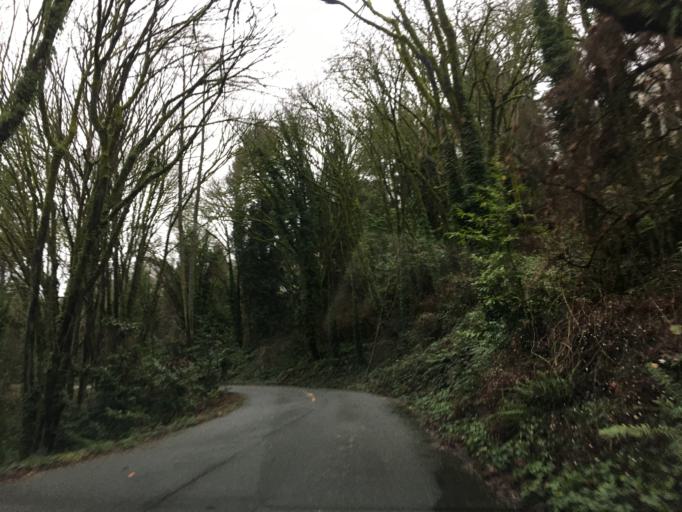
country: US
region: Washington
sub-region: King County
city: Seattle
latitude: 47.6395
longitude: -122.3145
